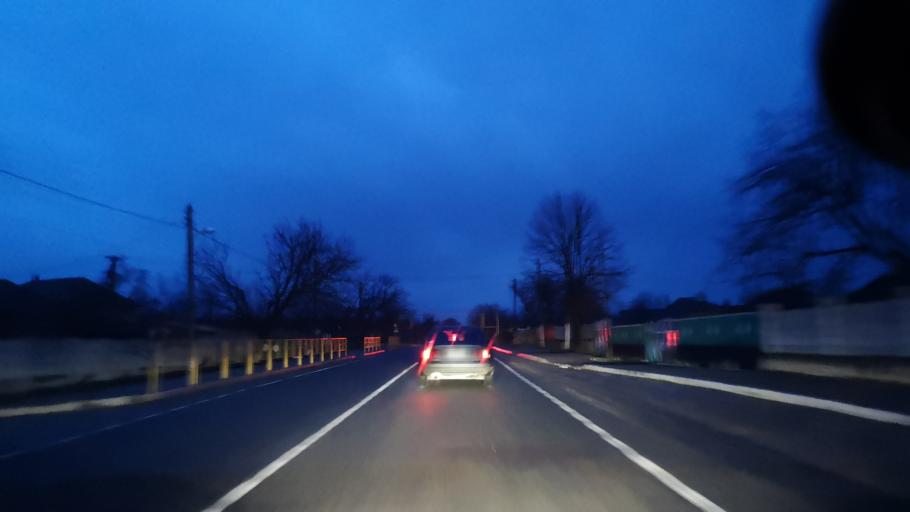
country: MD
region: Orhei
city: Orhei
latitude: 47.4348
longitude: 28.7982
